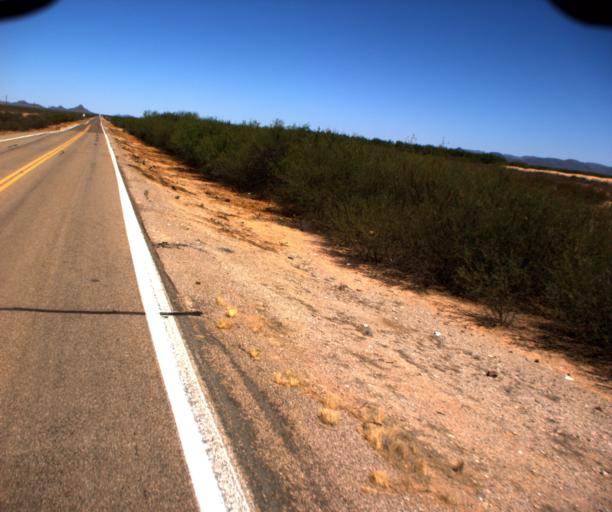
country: US
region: Arizona
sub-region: Pima County
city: Ajo
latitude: 32.1910
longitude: -112.4182
